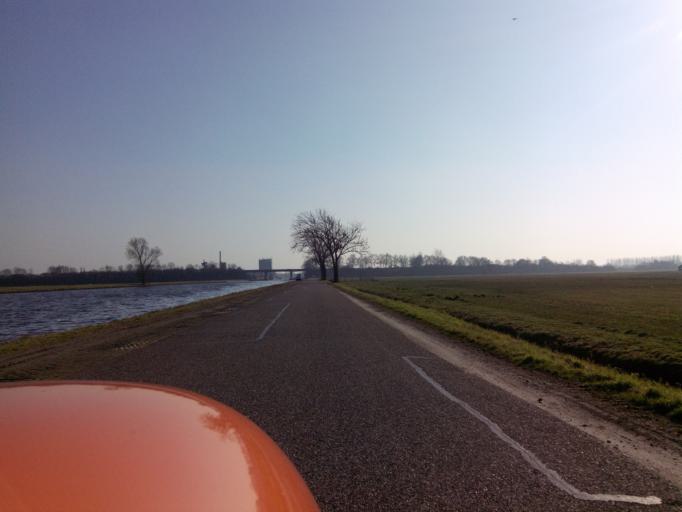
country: NL
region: Gelderland
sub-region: Gemeente Nijkerk
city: Nijkerk
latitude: 52.2457
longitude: 5.4689
